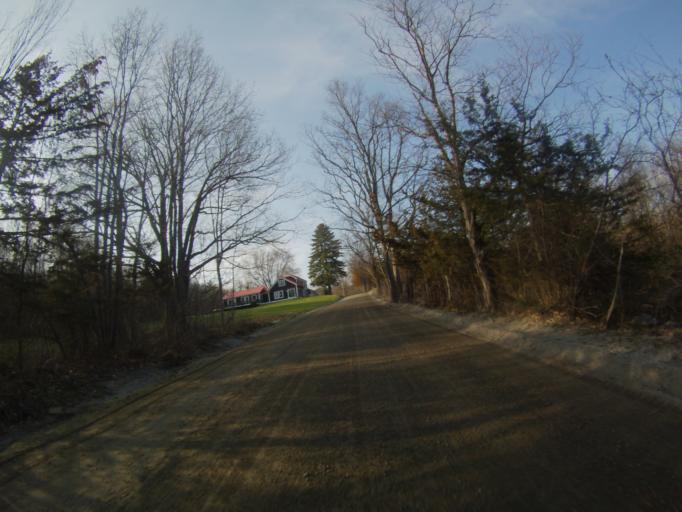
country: US
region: Vermont
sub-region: Addison County
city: Middlebury (village)
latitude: 44.0255
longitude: -73.2597
